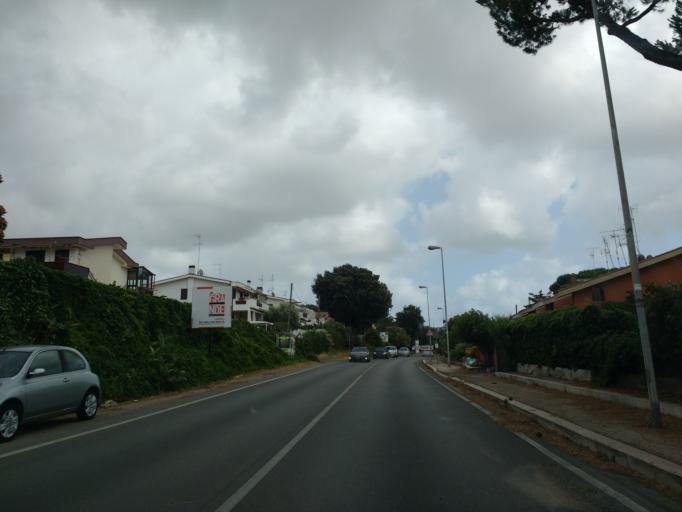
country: IT
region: Latium
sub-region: Citta metropolitana di Roma Capitale
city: Anzio
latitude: 41.4824
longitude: 12.6032
